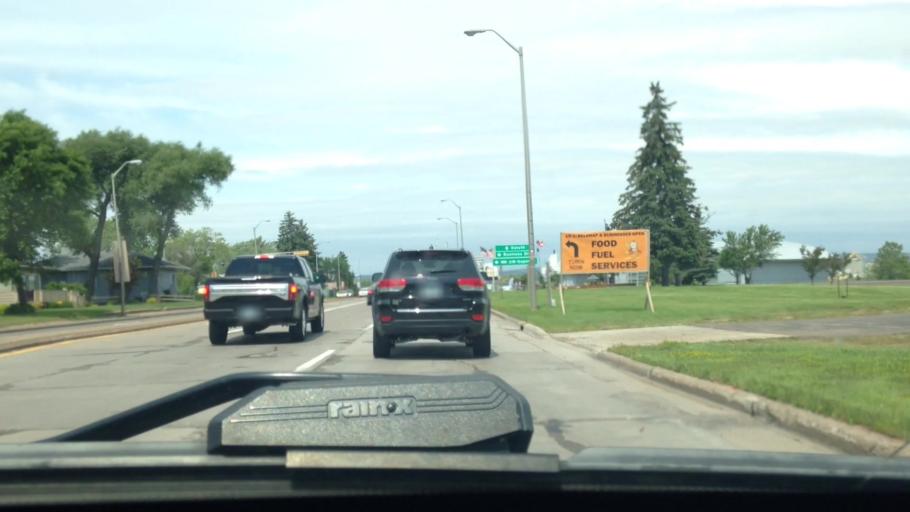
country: US
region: Wisconsin
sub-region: Douglas County
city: Superior
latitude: 46.7216
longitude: -92.0670
